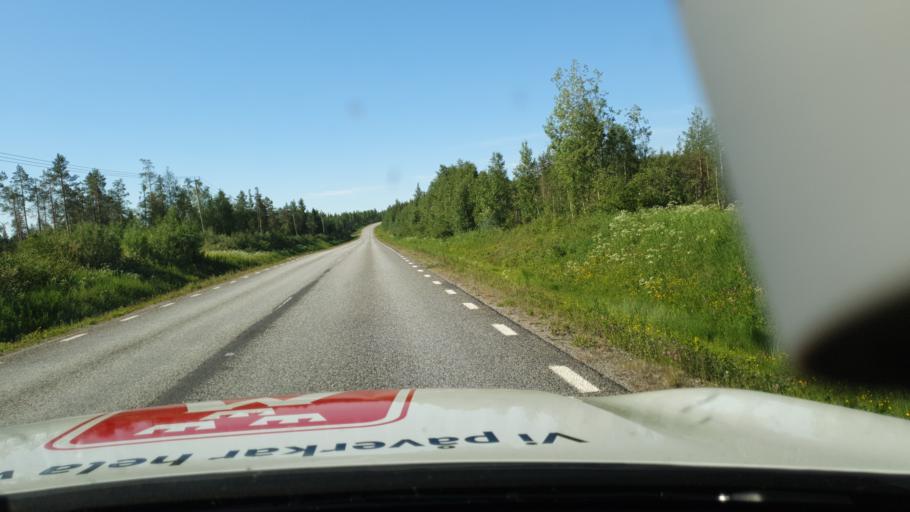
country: SE
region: Vaesterbotten
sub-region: Lycksele Kommun
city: Lycksele
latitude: 64.5487
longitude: 18.5077
